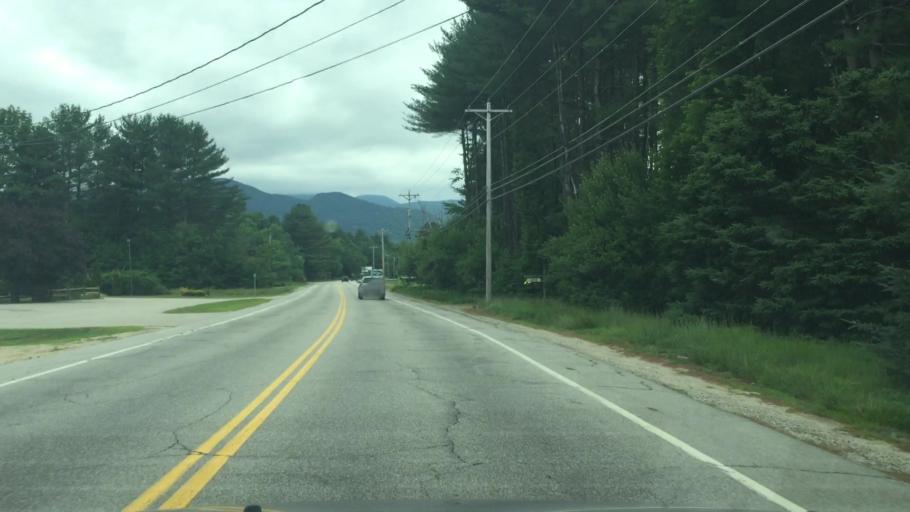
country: US
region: New Hampshire
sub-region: Carroll County
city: North Conway
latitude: 44.0803
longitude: -71.2557
